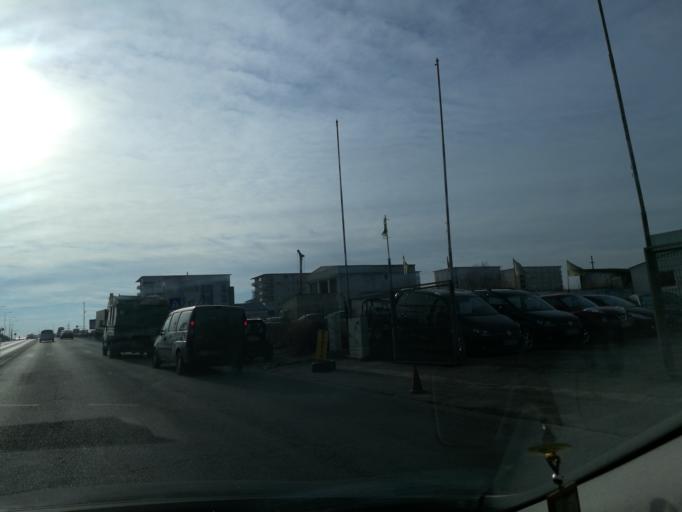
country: RO
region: Constanta
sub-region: Municipiul Constanta
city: Palazu Mare
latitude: 44.2013
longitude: 28.6084
